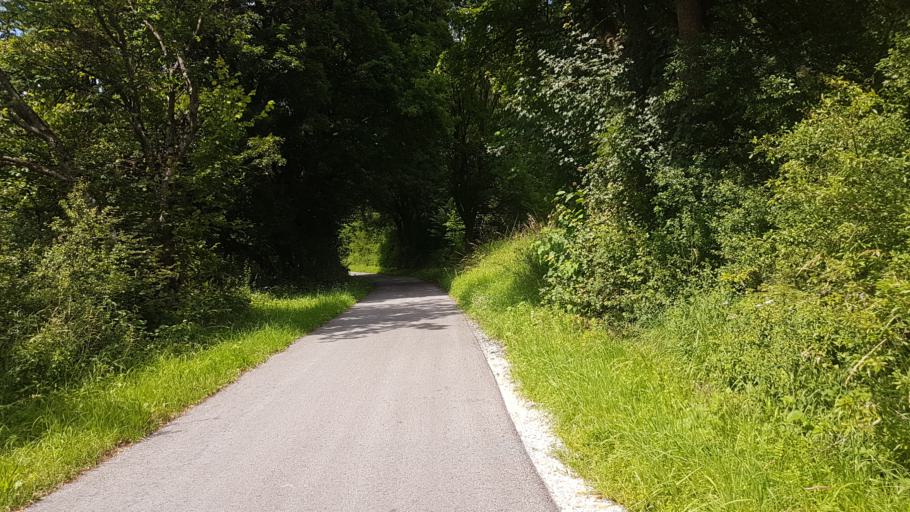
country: DE
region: Bavaria
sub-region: Regierungsbezirk Mittelfranken
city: Solnhofen
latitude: 48.9057
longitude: 10.9942
